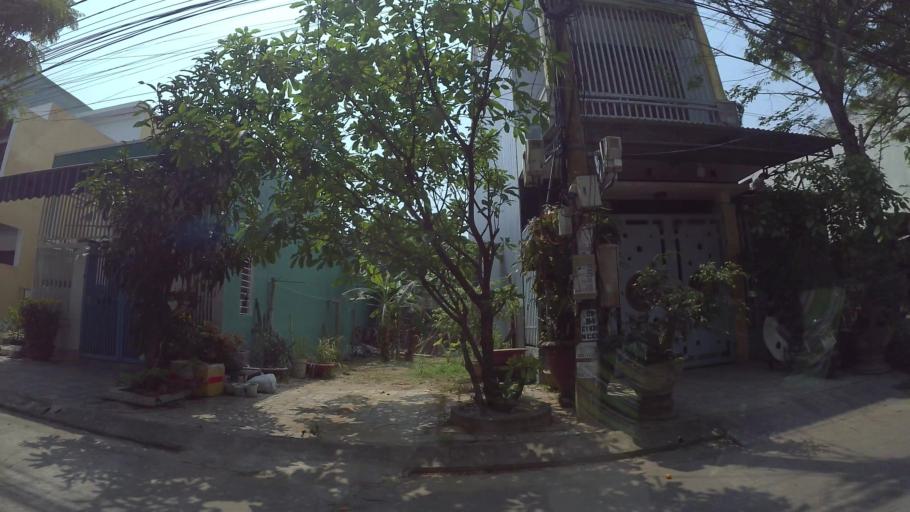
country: VN
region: Da Nang
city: Cam Le
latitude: 16.0038
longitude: 108.2094
